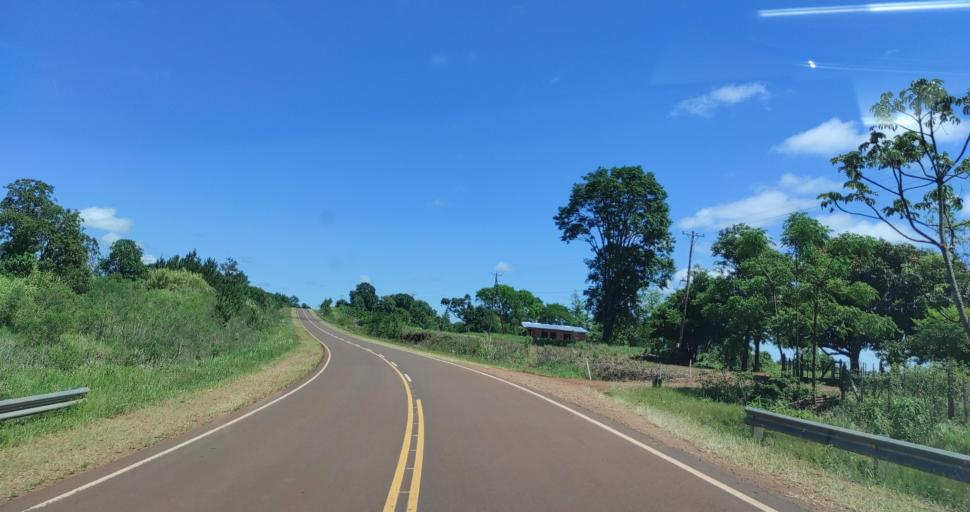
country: AR
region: Misiones
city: Campo Grande
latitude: -27.3253
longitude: -54.8921
